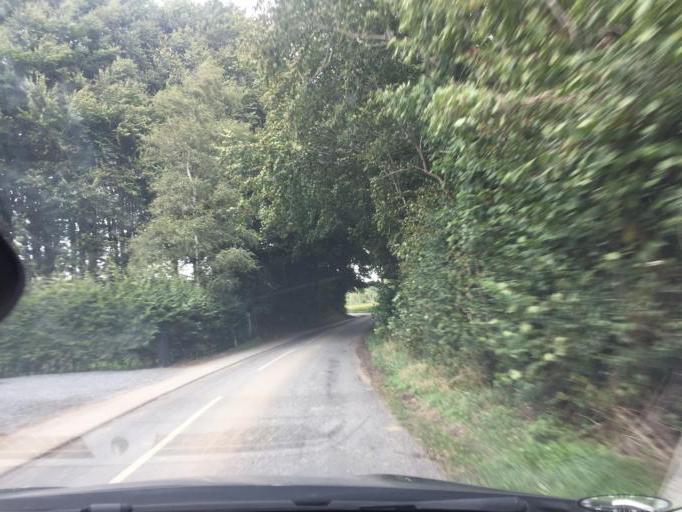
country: DK
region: South Denmark
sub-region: Assens Kommune
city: Arup
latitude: 55.3655
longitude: 10.0844
